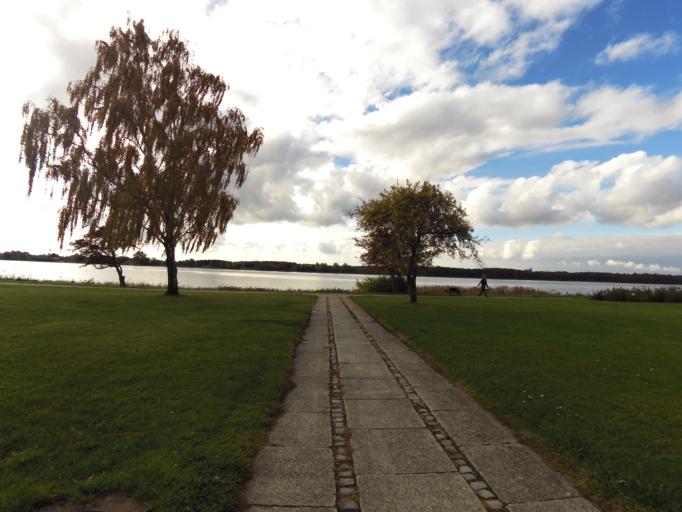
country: DK
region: Zealand
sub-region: Guldborgsund Kommune
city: Nykobing Falster
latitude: 54.7813
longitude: 11.8532
